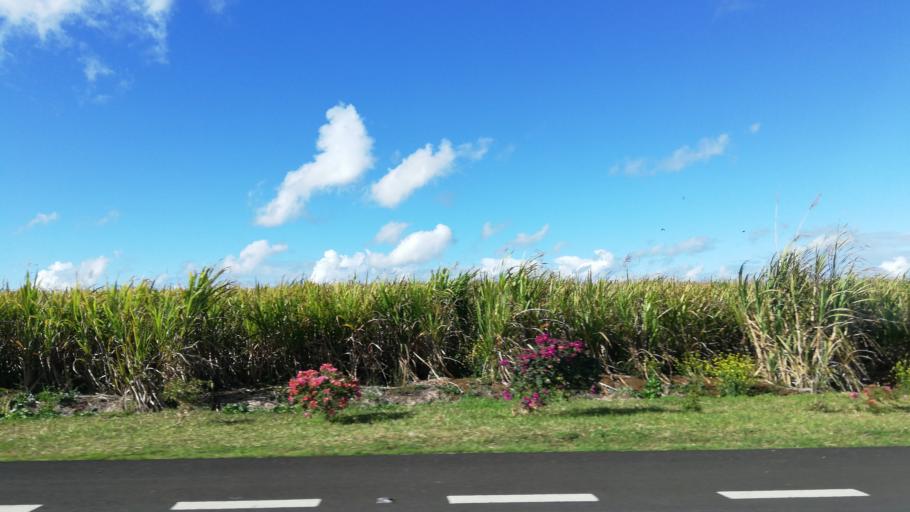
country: MU
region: Moka
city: Saint Pierre
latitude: -20.2323
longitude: 57.5202
